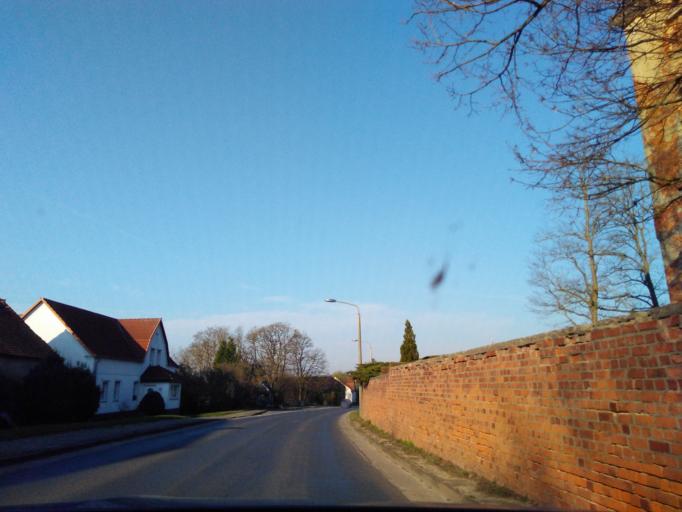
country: DE
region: Brandenburg
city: Protzel
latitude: 52.5695
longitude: 13.9928
